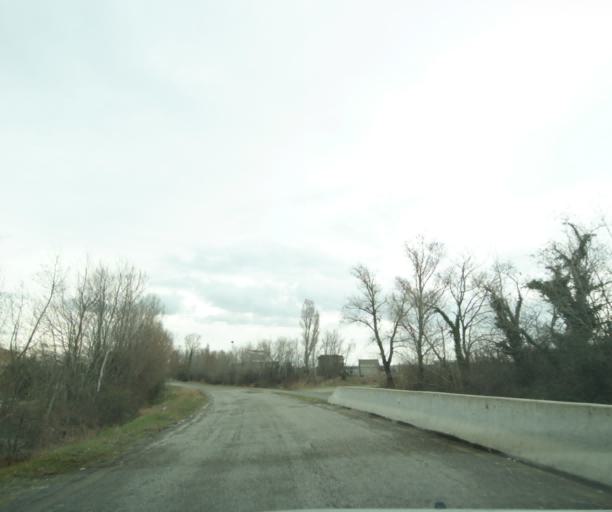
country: FR
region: Rhone-Alpes
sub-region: Departement de l'Ardeche
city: Cornas
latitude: 44.9738
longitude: 4.8622
